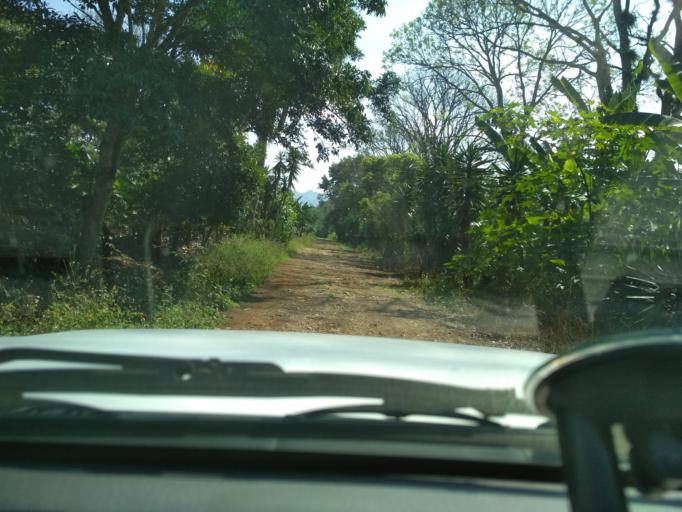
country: MX
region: Veracruz
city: Monte Blanco
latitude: 18.9780
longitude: -97.0122
